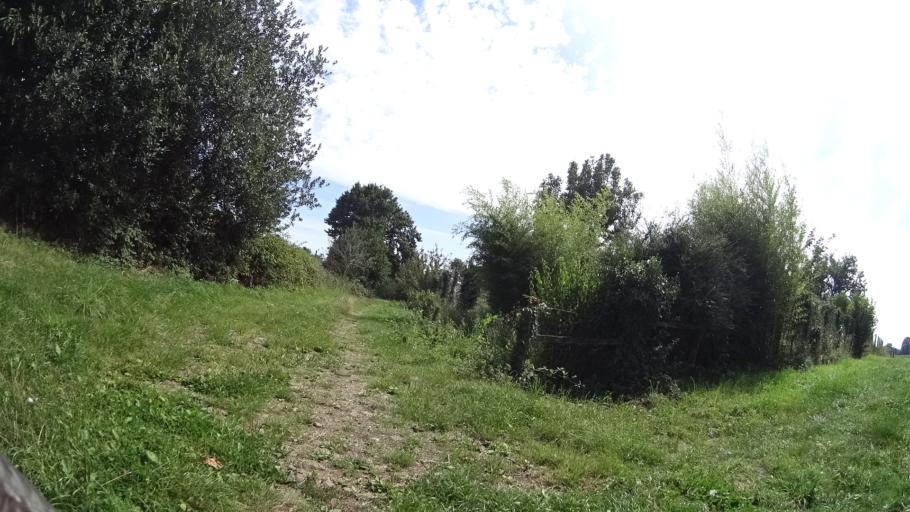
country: FR
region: Brittany
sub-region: Departement d'Ille-et-Vilaine
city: La Meziere
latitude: 48.2292
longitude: -1.7468
